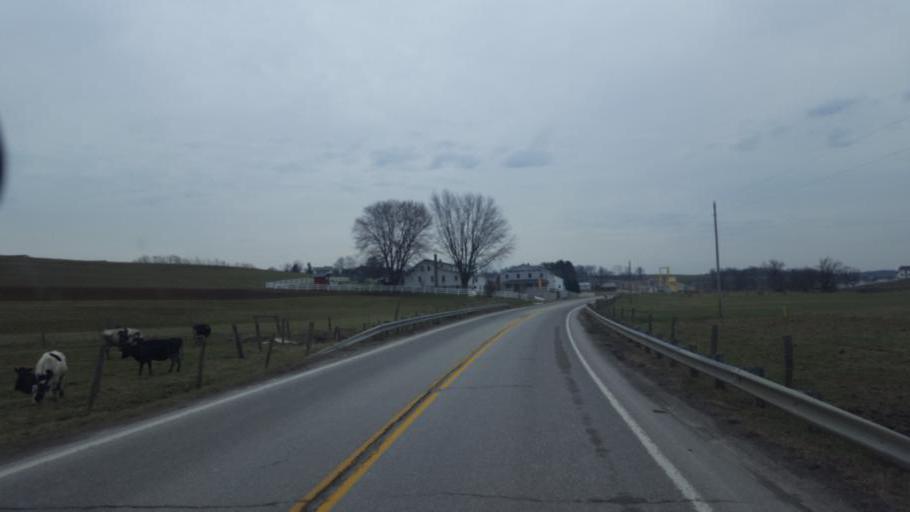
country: US
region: Ohio
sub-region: Tuscarawas County
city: Sugarcreek
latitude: 40.4856
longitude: -81.7419
